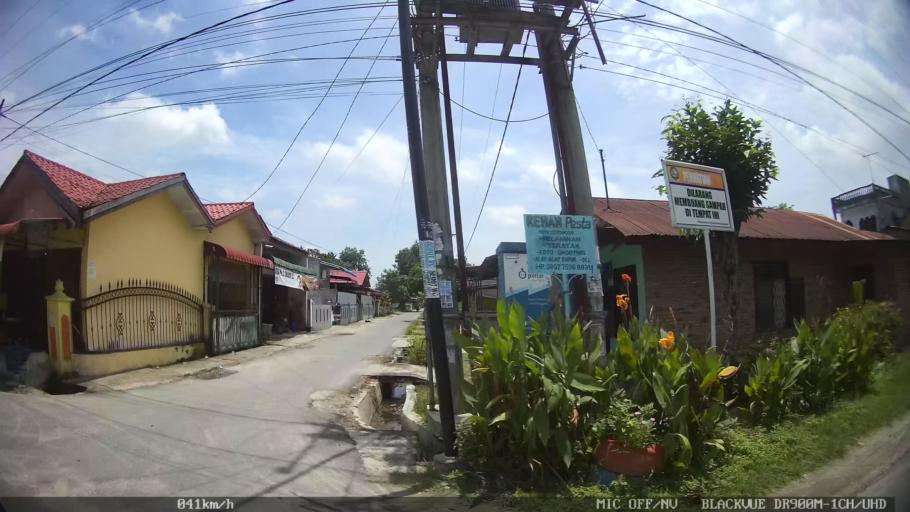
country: ID
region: North Sumatra
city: Percut
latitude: 3.5474
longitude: 98.8731
